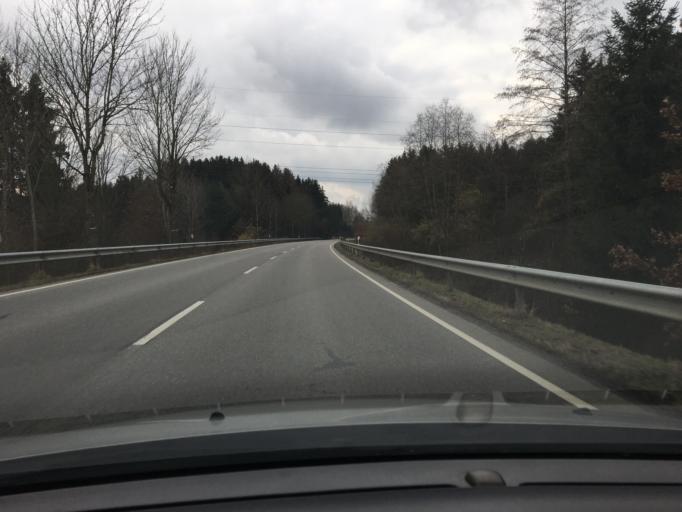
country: DE
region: Bavaria
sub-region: Lower Bavaria
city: Furth
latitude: 48.4356
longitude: 12.4117
